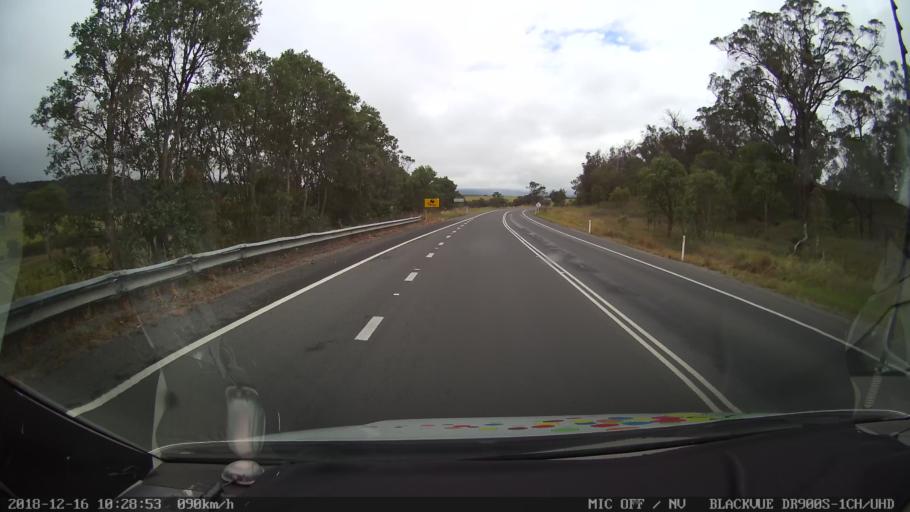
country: AU
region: New South Wales
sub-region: Tenterfield Municipality
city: Carrolls Creek
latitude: -29.1157
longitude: 151.9959
